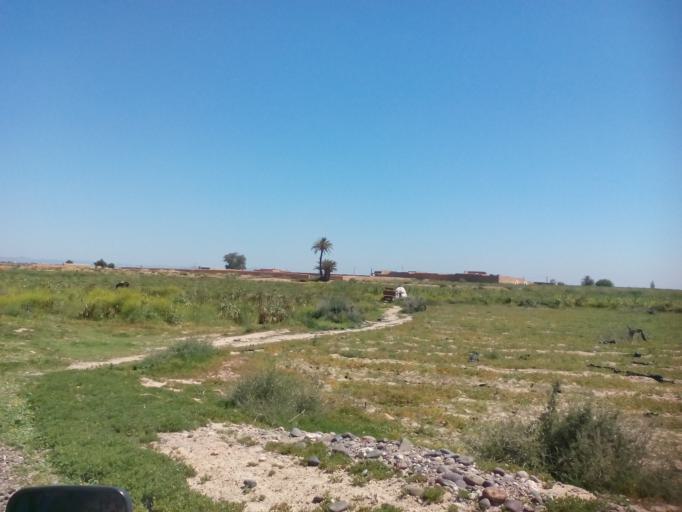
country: MA
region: Marrakech-Tensift-Al Haouz
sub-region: Marrakech
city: Marrakesh
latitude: 31.6428
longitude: -8.3017
